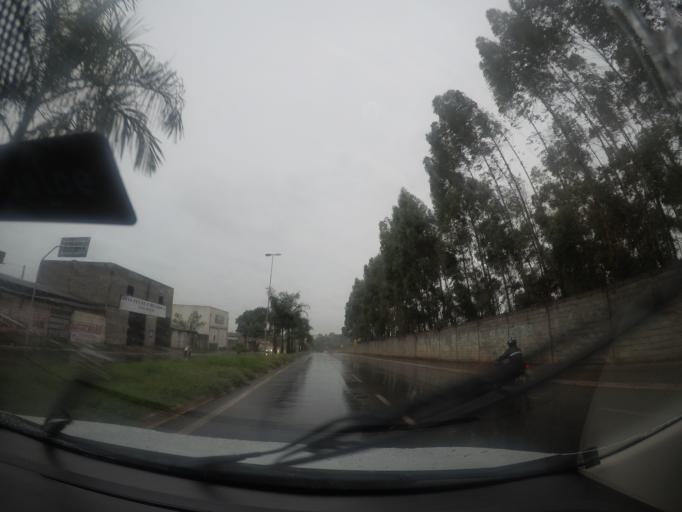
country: BR
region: Goias
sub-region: Goiania
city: Goiania
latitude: -16.6339
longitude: -49.3227
